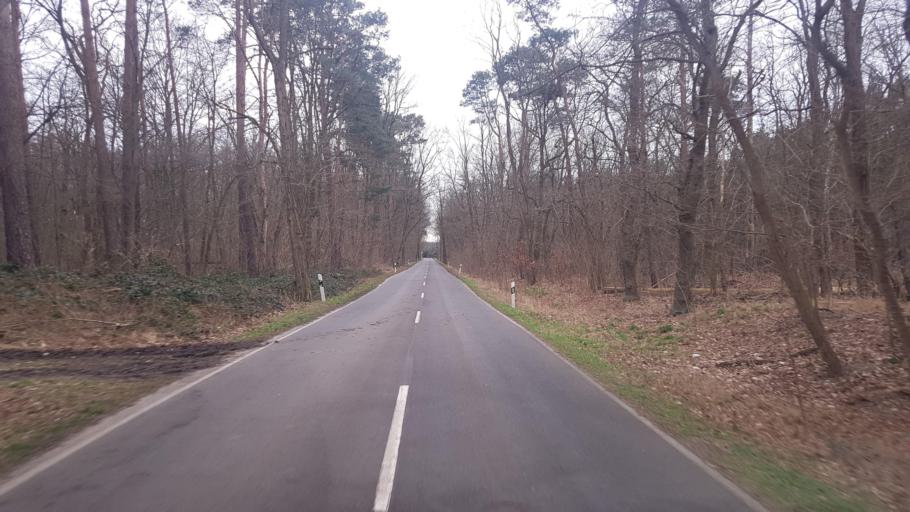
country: DE
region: Brandenburg
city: Halbe
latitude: 52.0767
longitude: 13.6945
